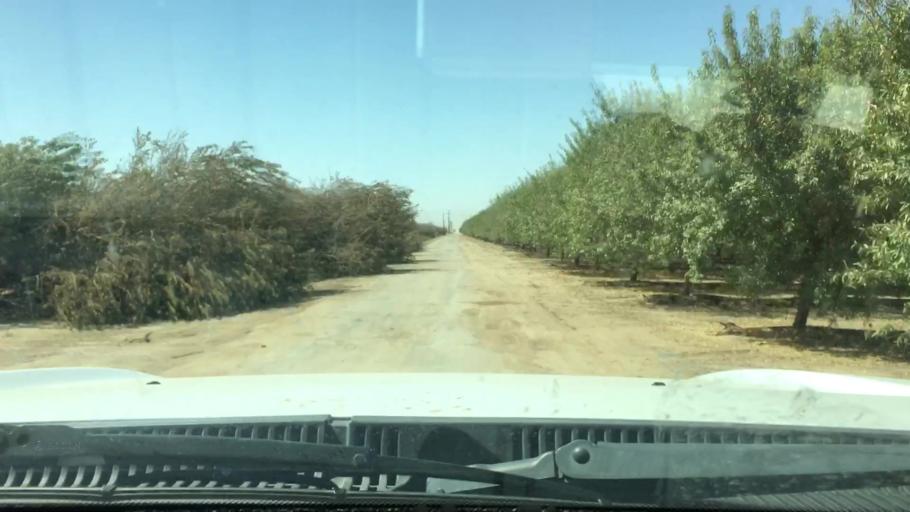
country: US
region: California
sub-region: Kern County
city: Shafter
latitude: 35.4563
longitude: -119.3092
